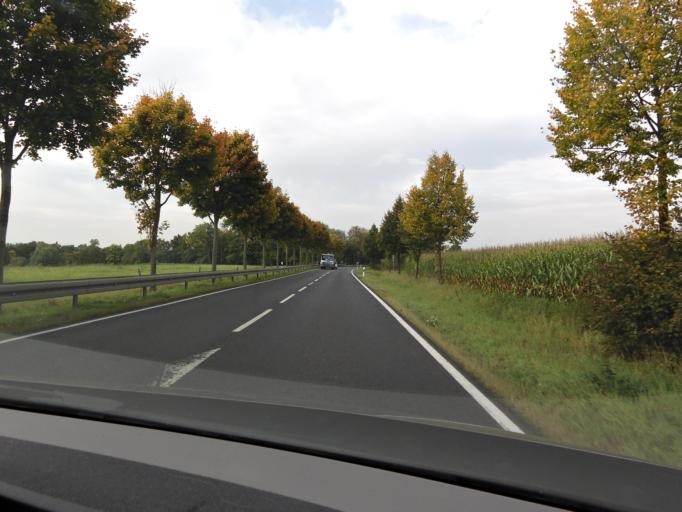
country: DE
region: Thuringia
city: Breitungen
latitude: 50.7786
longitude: 10.3117
